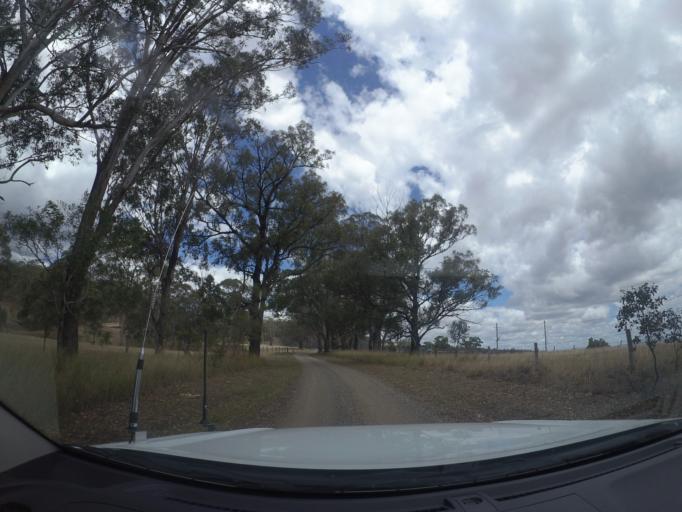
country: AU
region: Queensland
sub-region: Logan
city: Cedar Vale
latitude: -27.9158
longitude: 153.0311
